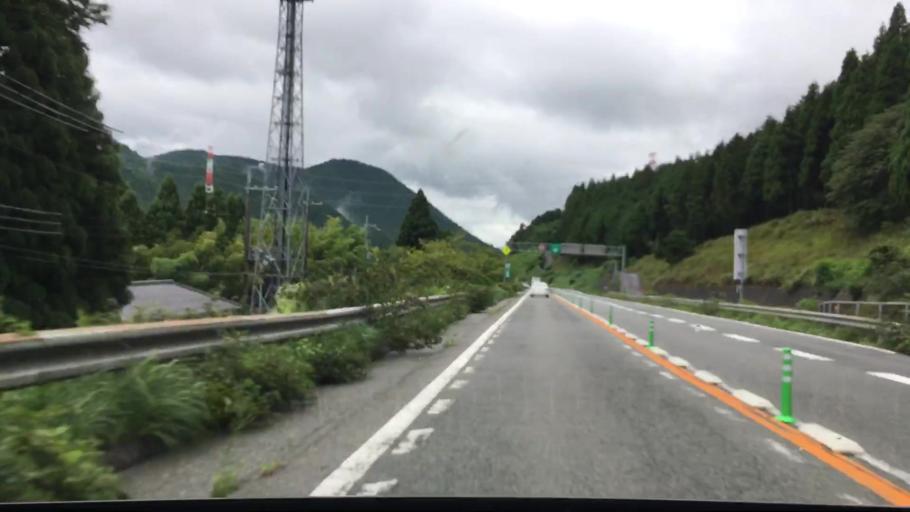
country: JP
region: Hyogo
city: Nishiwaki
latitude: 35.1233
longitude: 134.7871
